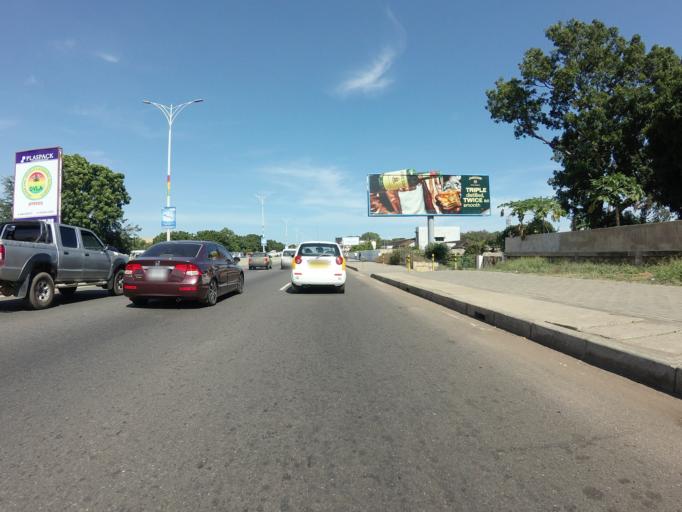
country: GH
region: Greater Accra
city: Accra
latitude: 5.5884
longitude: -0.1794
